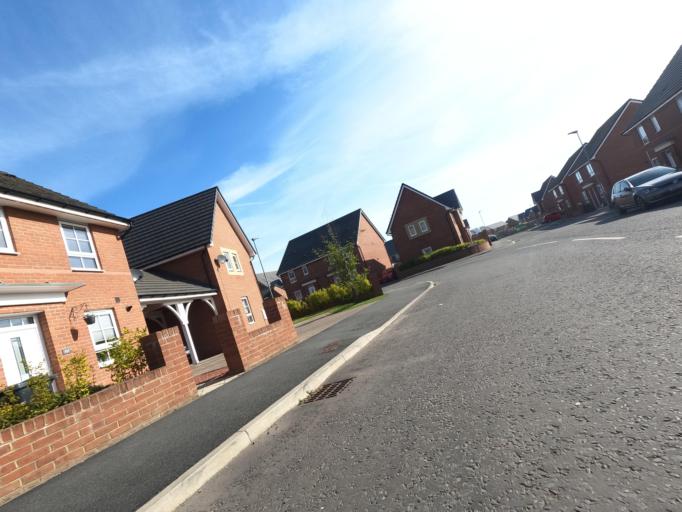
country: GB
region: England
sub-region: Northumberland
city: Morpeth
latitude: 55.1569
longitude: -1.6726
